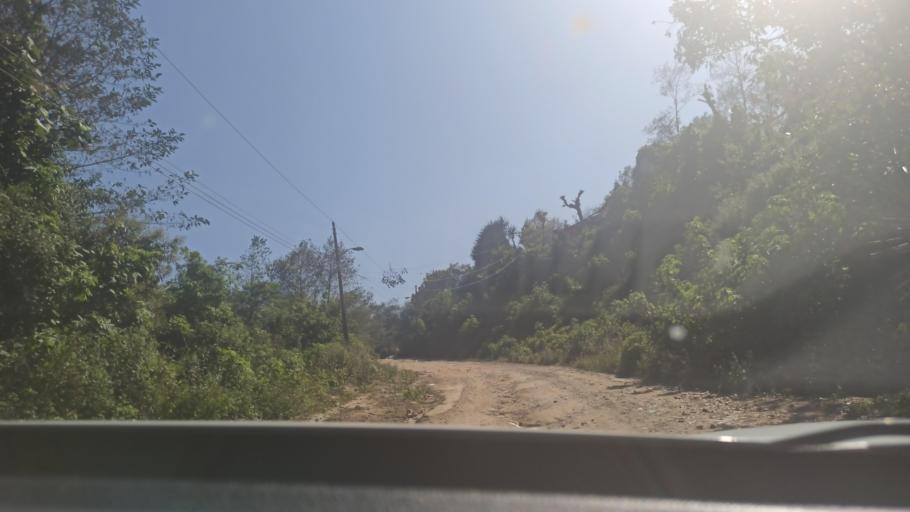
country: MX
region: Veracruz
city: Xocotla
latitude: 18.9684
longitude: -97.0896
